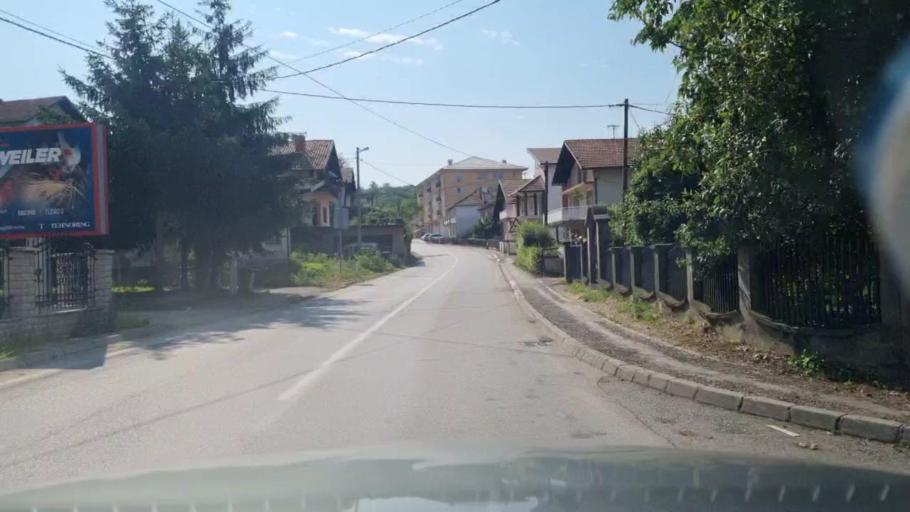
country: BA
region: Federation of Bosnia and Herzegovina
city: Gradacac
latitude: 44.8766
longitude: 18.4333
